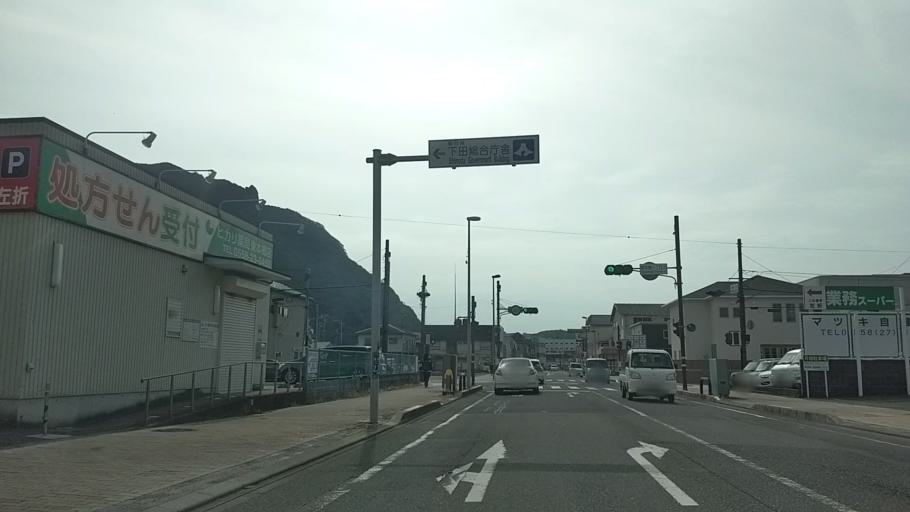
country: JP
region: Shizuoka
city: Shimoda
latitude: 34.6828
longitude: 138.9457
